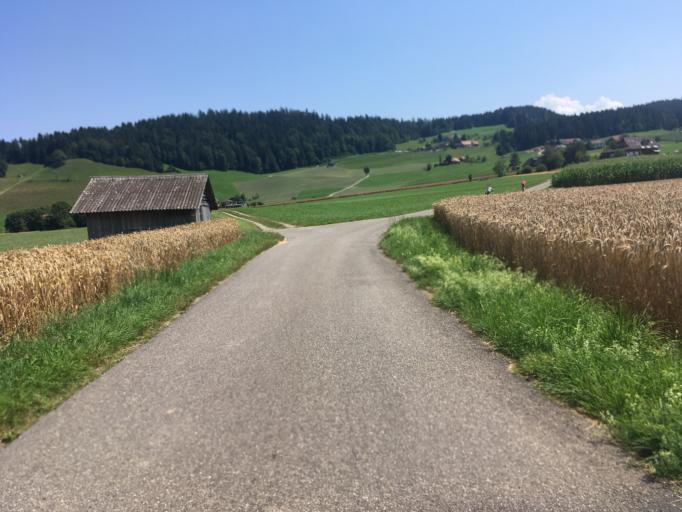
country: CH
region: Bern
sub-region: Bern-Mittelland District
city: Bowil
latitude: 46.8996
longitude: 7.7028
